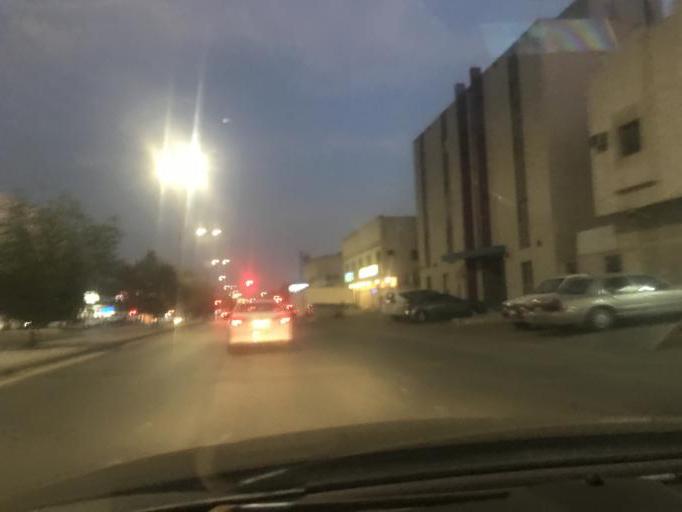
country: SA
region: Ar Riyad
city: Riyadh
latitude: 24.7321
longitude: 46.7613
